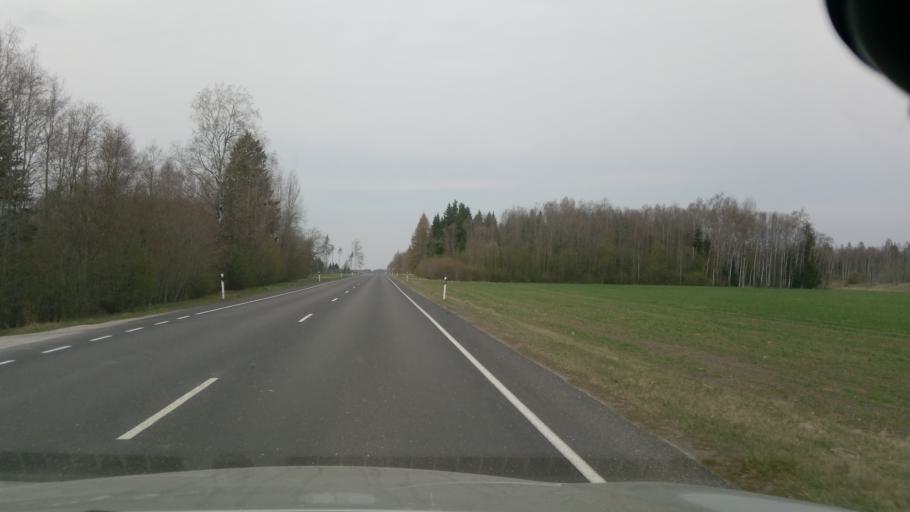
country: EE
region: Viljandimaa
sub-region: Vohma linn
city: Vohma
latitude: 58.7141
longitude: 25.6133
